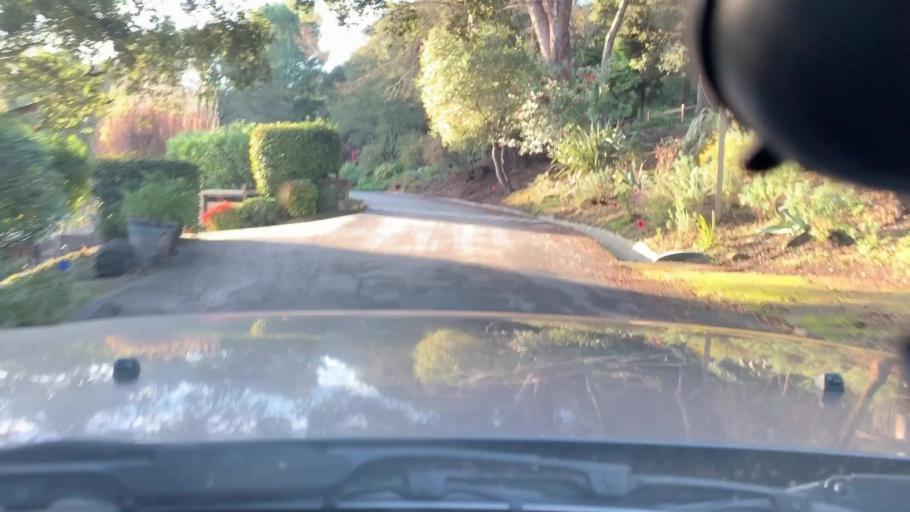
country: US
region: California
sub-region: San Mateo County
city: Portola Valley
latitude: 37.3976
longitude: -122.2497
